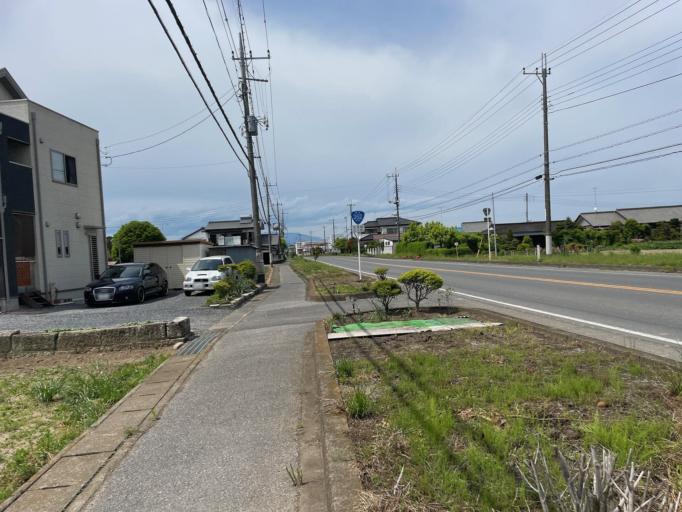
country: JP
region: Tochigi
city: Mibu
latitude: 36.4618
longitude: 139.7701
